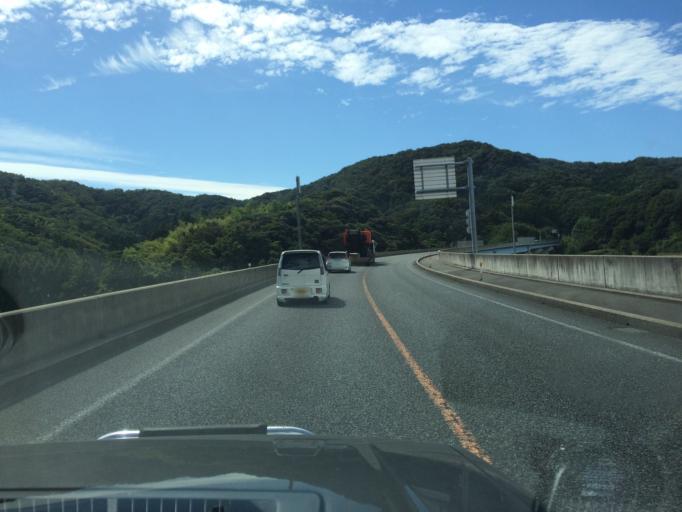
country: JP
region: Tottori
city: Tottori
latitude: 35.5169
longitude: 134.0244
